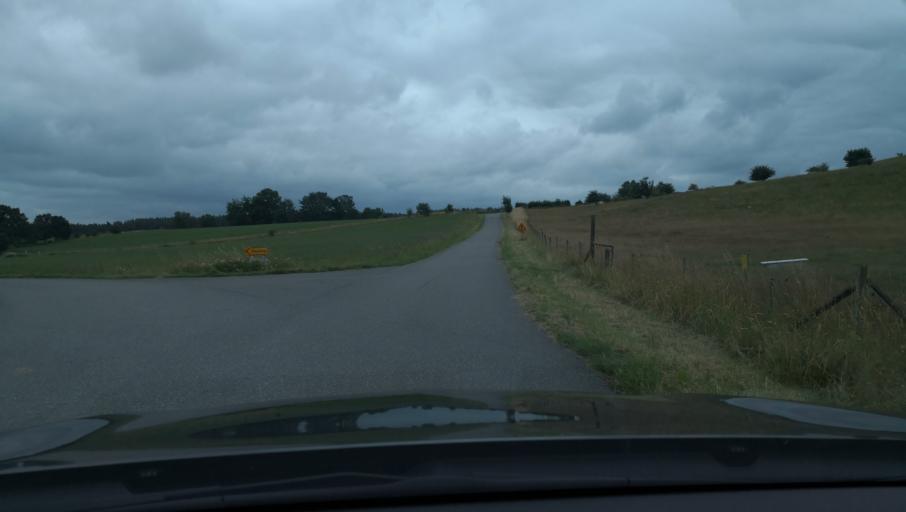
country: SE
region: Skane
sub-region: Simrishamns Kommun
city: Kivik
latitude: 55.7258
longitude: 14.1672
